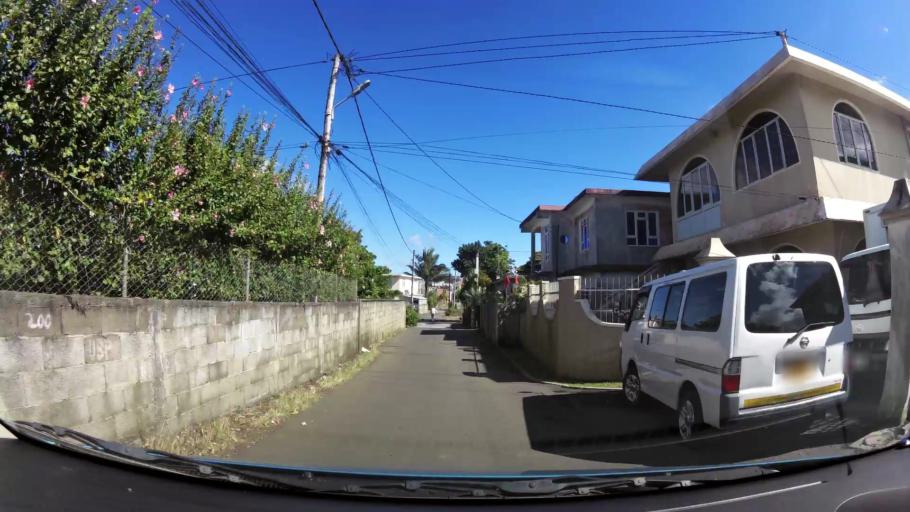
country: MU
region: Plaines Wilhems
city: Vacoas
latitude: -20.3171
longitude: 57.4878
